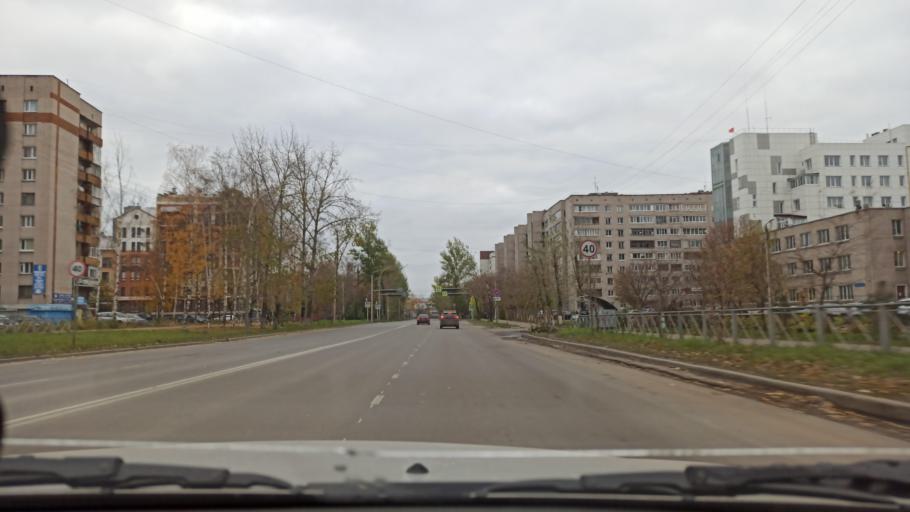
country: RU
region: Vologda
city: Vologda
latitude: 59.2153
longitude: 39.8757
